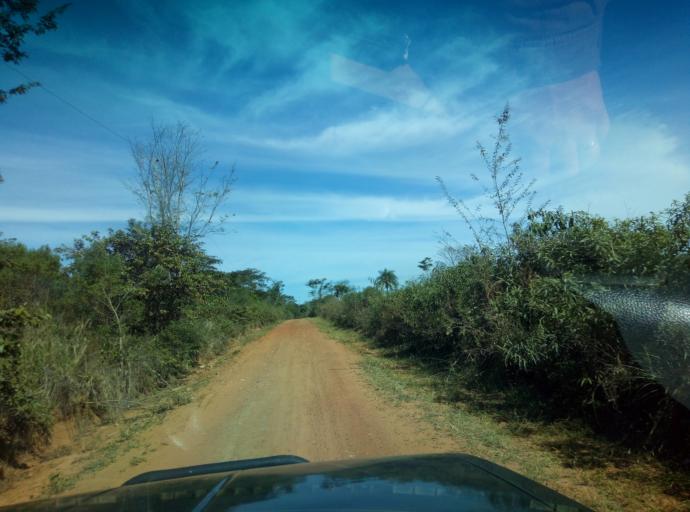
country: PY
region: Caaguazu
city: Carayao
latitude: -25.1857
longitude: -56.2547
